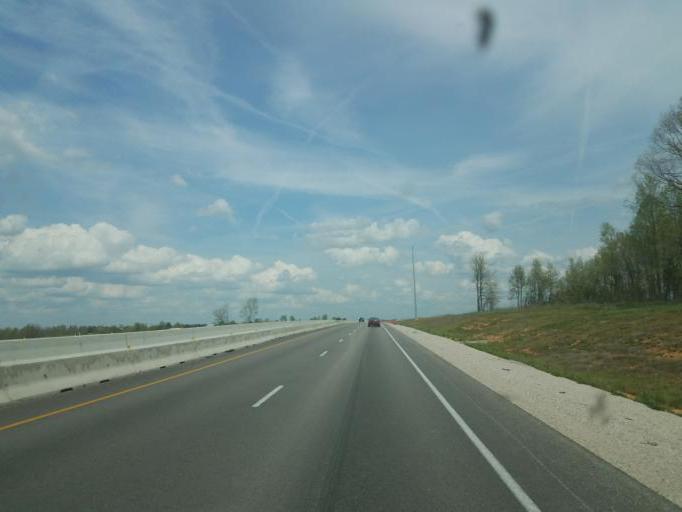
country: US
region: Kentucky
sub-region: Larue County
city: Hodgenville
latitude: 37.4798
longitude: -85.8811
